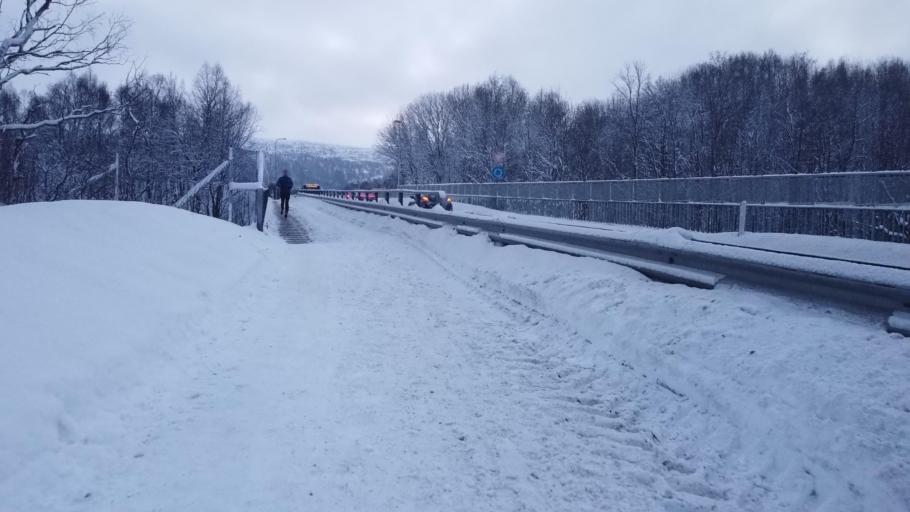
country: NO
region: Nordland
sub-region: Rana
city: Mo i Rana
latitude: 66.3259
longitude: 14.1590
